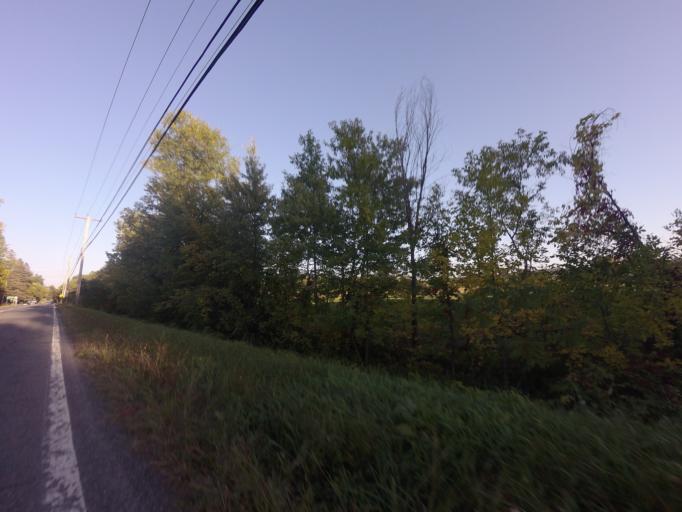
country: CA
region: Quebec
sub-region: Monteregie
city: Rigaud
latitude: 45.4803
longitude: -74.2635
